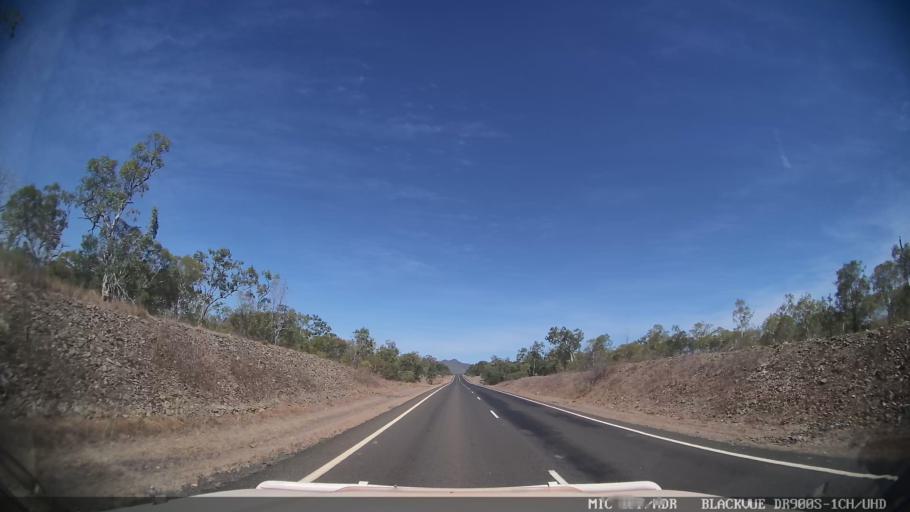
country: AU
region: Queensland
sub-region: Cook
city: Cooktown
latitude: -15.7010
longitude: 144.6063
